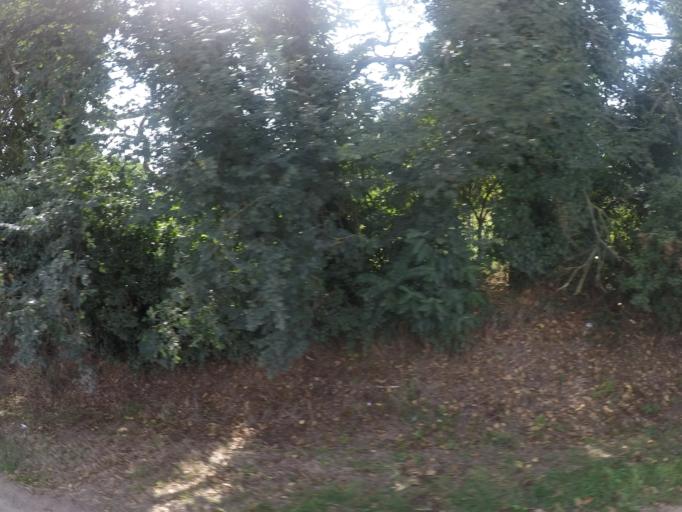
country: FR
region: Brittany
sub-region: Departement des Cotes-d'Armor
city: Goudelin
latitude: 48.6008
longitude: -3.0301
